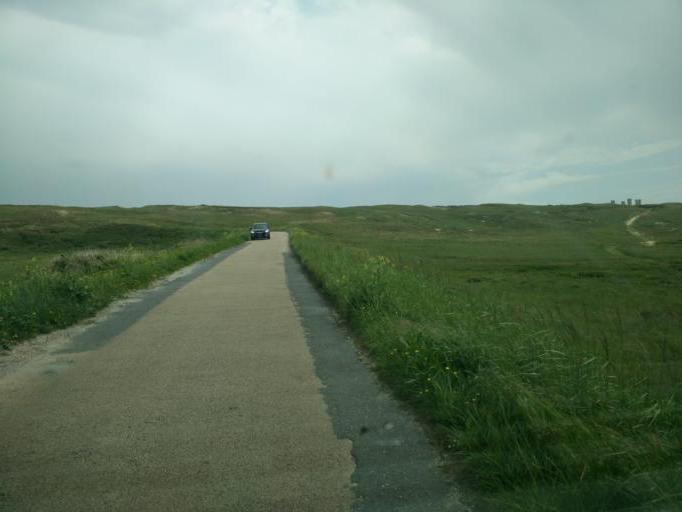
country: FR
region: Brittany
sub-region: Departement du Finistere
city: Camaret-sur-Mer
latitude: 48.2785
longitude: -4.6146
